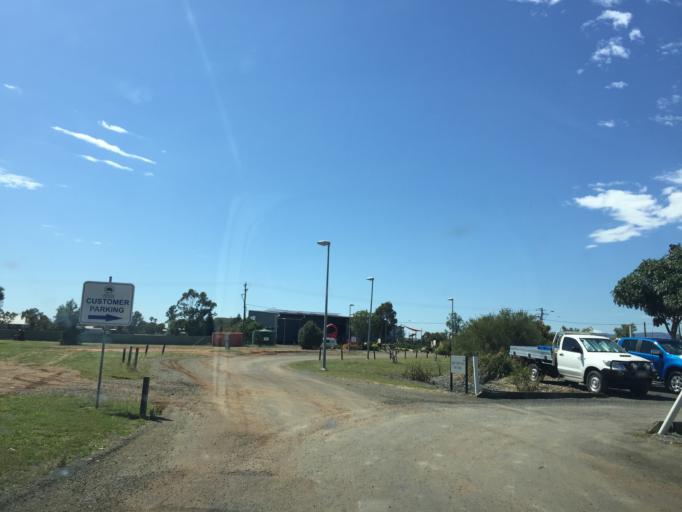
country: AU
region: Queensland
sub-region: Central Highlands
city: Blackwater
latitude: -23.5850
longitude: 148.8728
